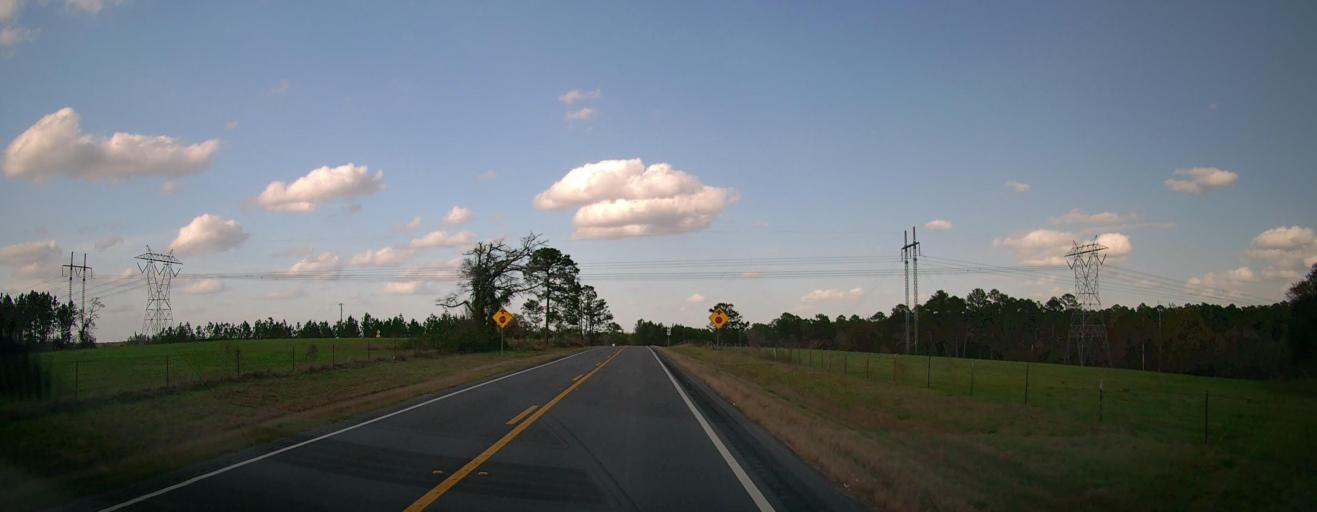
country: US
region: Georgia
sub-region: Wheeler County
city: Alamo
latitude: 32.1198
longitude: -82.7941
